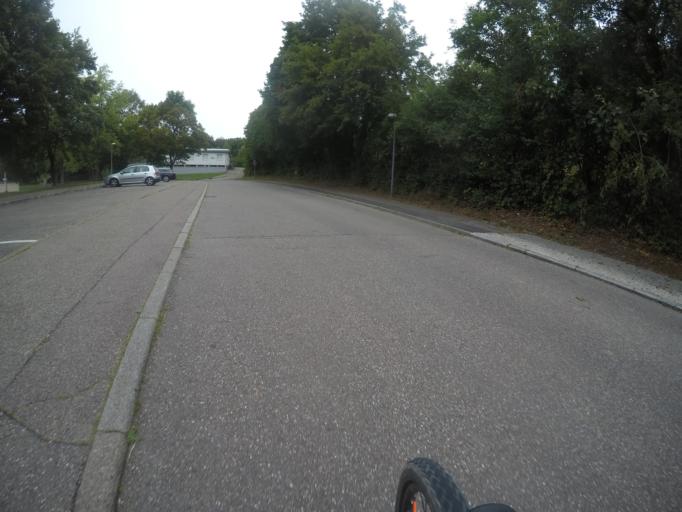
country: DE
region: Baden-Wuerttemberg
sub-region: Karlsruhe Region
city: Simmozheim
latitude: 48.7778
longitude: 8.8120
